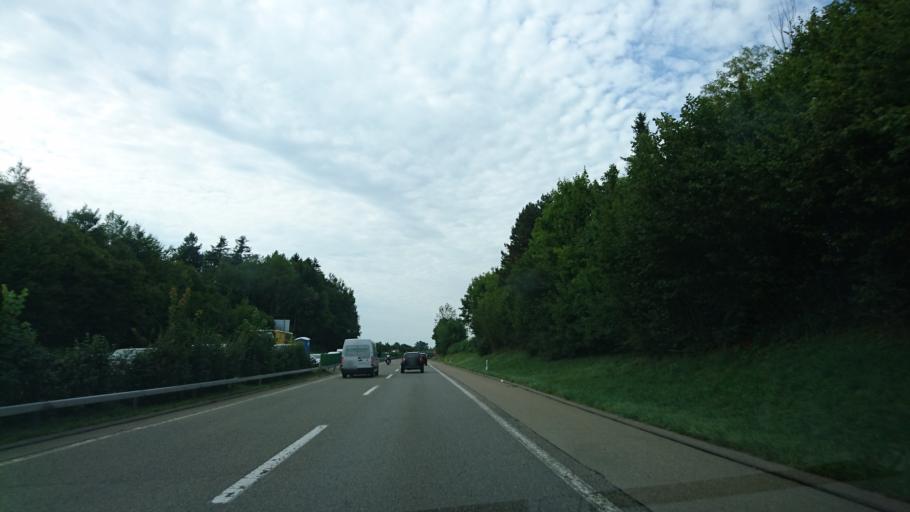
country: CH
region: Zurich
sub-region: Bezirk Hinwil
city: Bubikon
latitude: 47.2785
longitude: 8.8268
